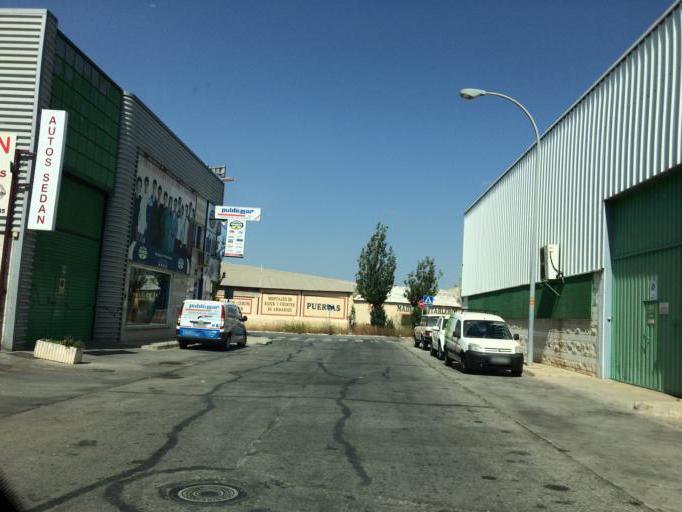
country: ES
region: Andalusia
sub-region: Provincia de Malaga
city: Malaga
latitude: 36.7084
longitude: -4.4712
